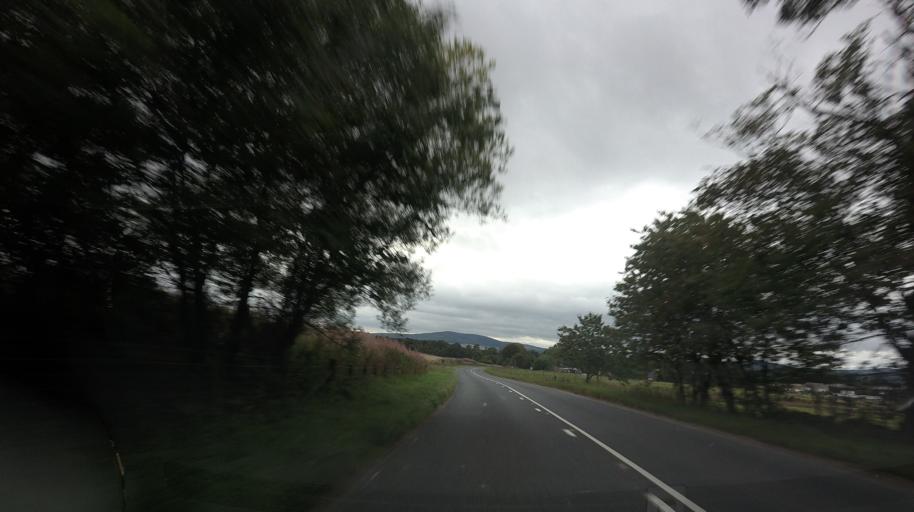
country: GB
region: Scotland
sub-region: Aberdeenshire
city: Kemnay
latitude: 57.1830
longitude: -2.4745
